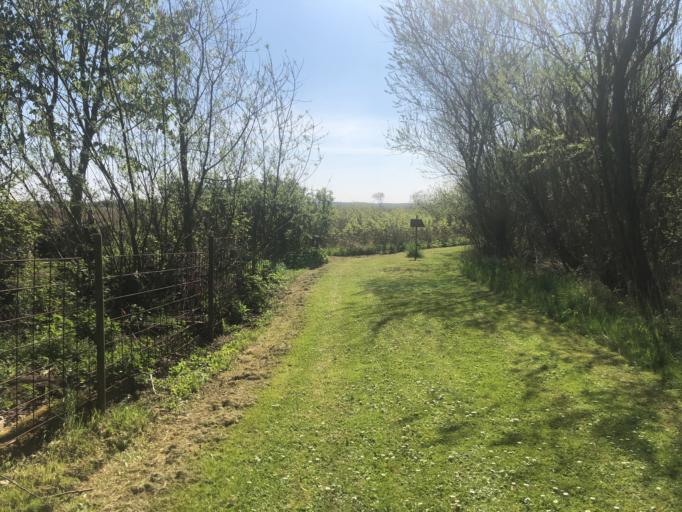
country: DK
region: Central Jutland
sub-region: Holstebro Kommune
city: Vinderup
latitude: 56.5719
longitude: 8.7900
